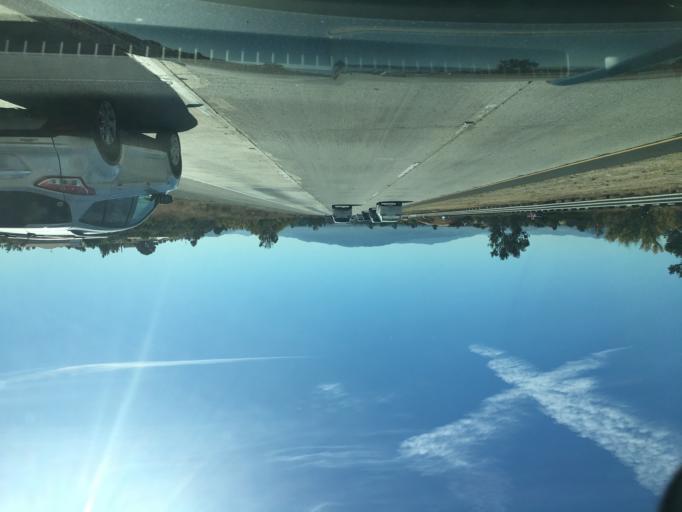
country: US
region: California
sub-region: Riverside County
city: Murrieta
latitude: 33.5861
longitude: -117.2344
